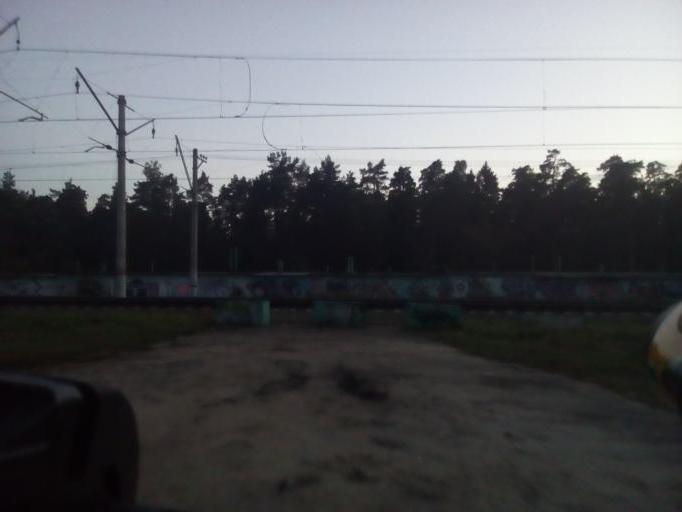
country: RU
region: Moskovskaya
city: Zhukovskiy
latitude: 55.5995
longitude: 38.1428
